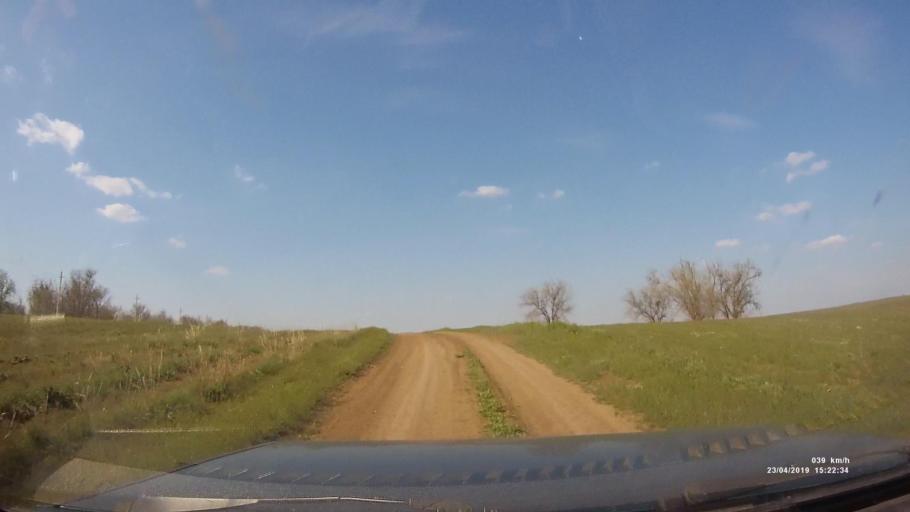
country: RU
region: Rostov
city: Remontnoye
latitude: 46.5298
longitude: 42.9702
